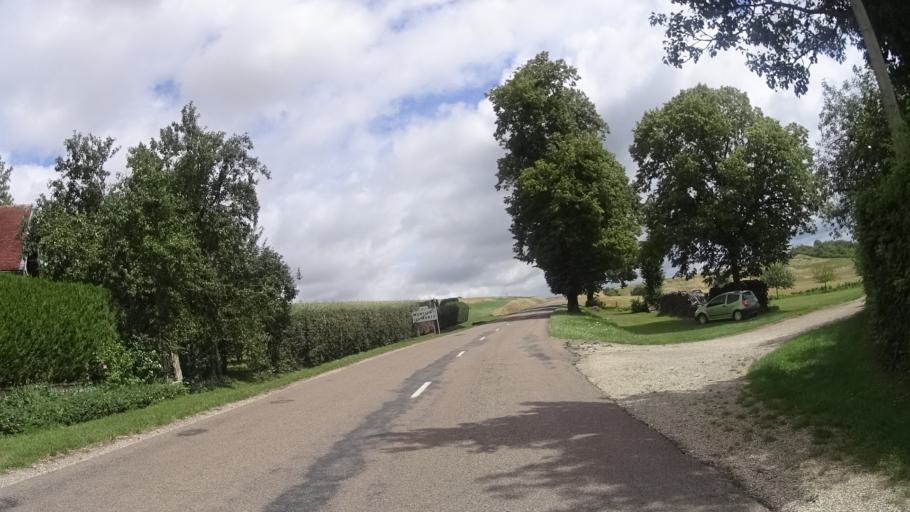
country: FR
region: Champagne-Ardenne
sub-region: Departement de l'Aube
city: Ervy-le-Chatel
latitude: 48.1050
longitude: 3.9473
